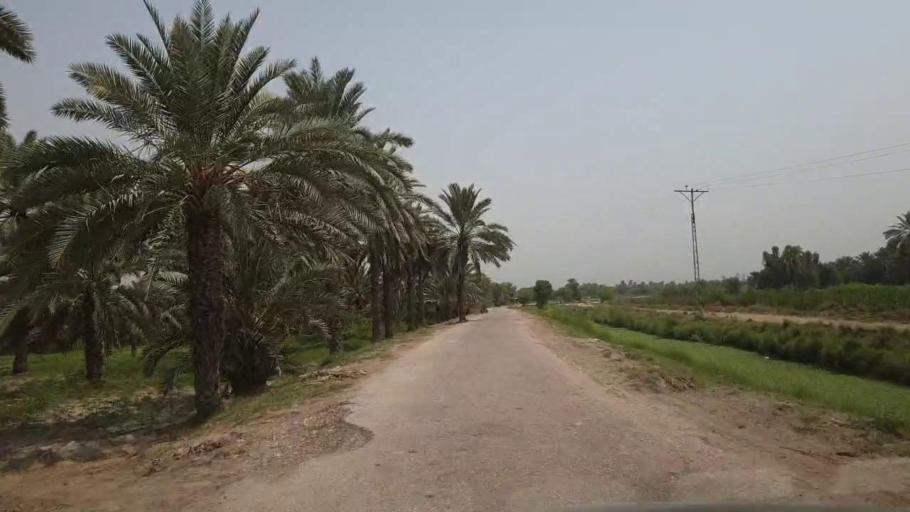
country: PK
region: Sindh
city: Gambat
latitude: 27.4202
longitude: 68.5538
